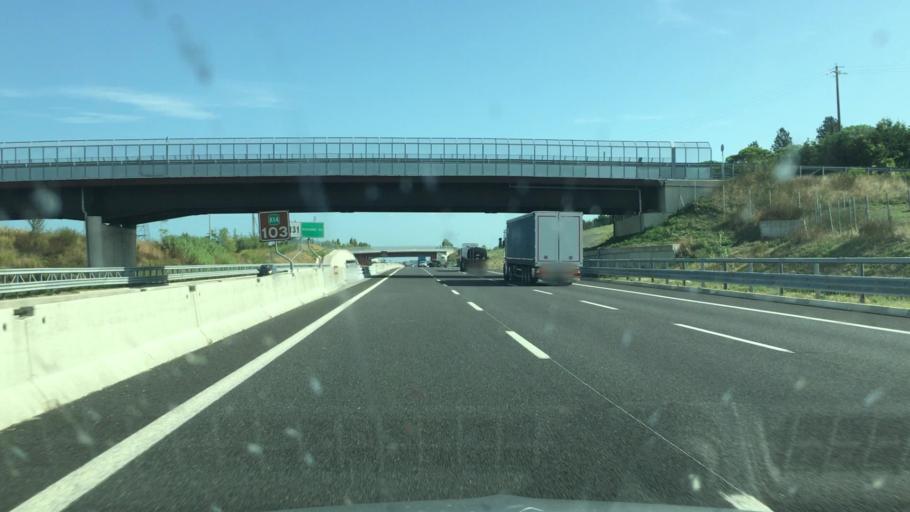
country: IT
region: Emilia-Romagna
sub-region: Provincia di Rimini
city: Rivazzurra
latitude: 44.0101
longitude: 12.5949
